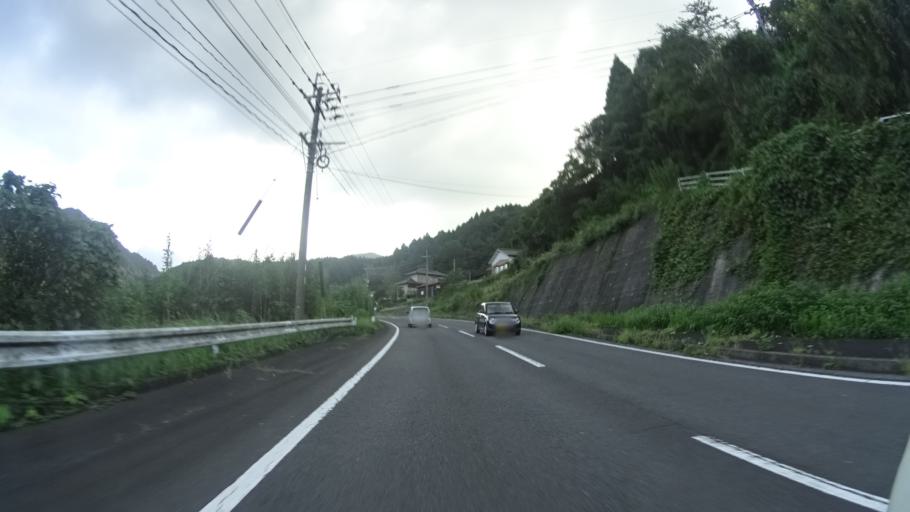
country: JP
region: Oita
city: Beppu
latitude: 33.3429
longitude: 131.4000
